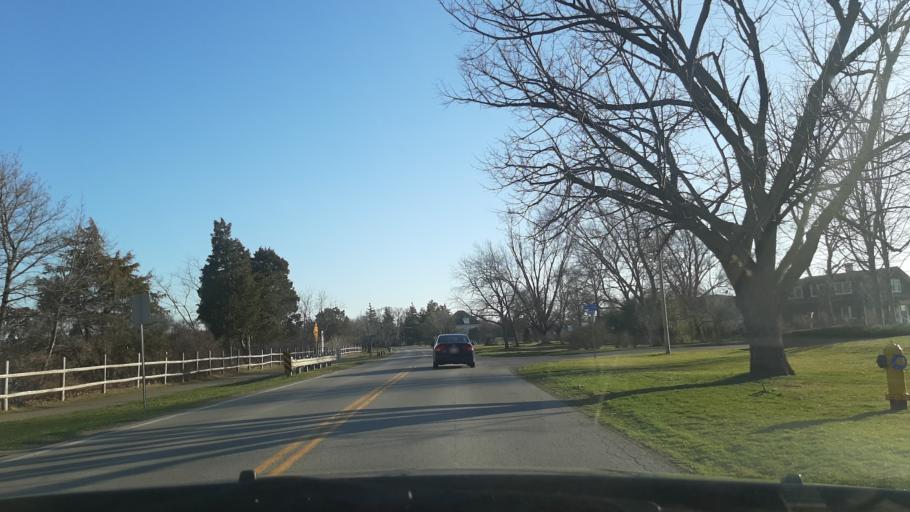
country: US
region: New York
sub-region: Niagara County
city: Lewiston
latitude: 43.1872
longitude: -79.0575
